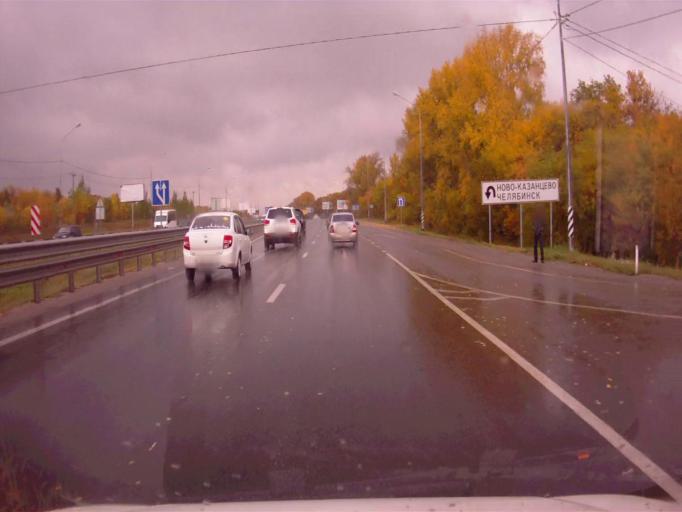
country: RU
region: Chelyabinsk
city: Dolgoderevenskoye
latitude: 55.2835
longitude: 61.3429
